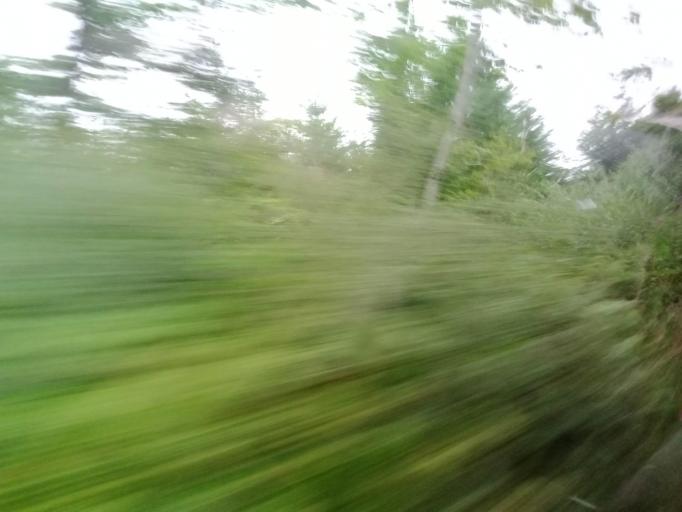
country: IE
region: Munster
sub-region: Waterford
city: Dungarvan
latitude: 52.0466
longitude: -7.6548
